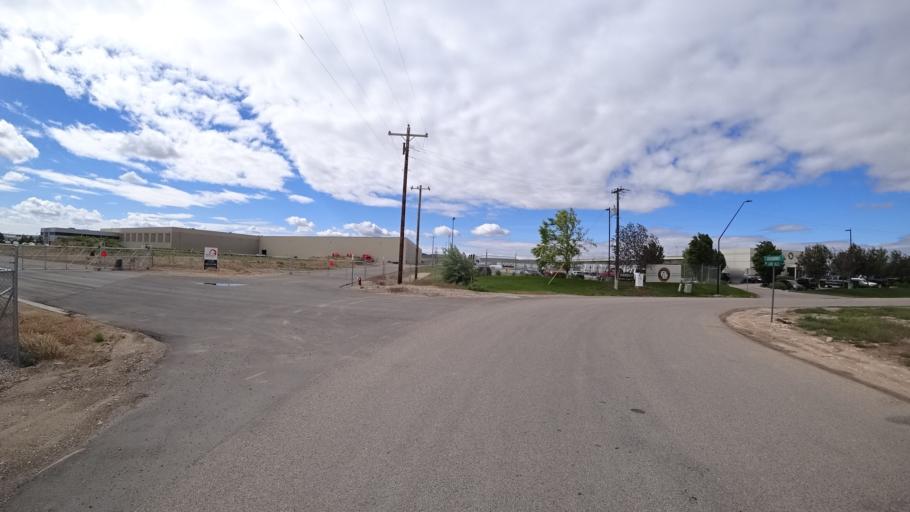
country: US
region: Idaho
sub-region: Ada County
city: Boise
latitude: 43.5462
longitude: -116.1939
